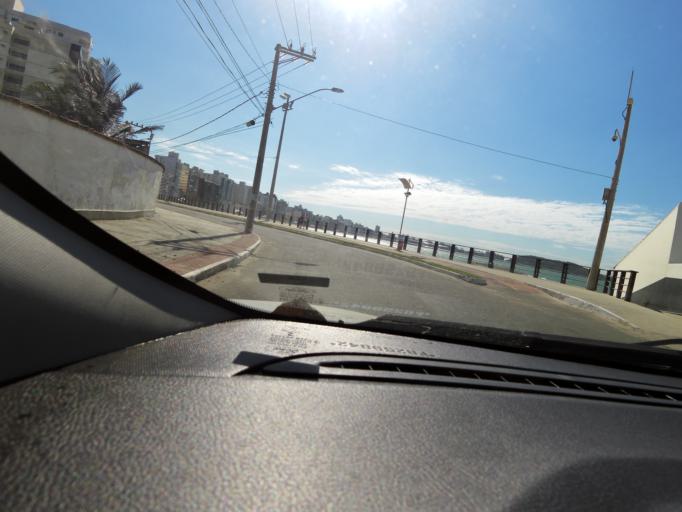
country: BR
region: Espirito Santo
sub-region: Guarapari
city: Guarapari
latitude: -20.6623
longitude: -40.4956
